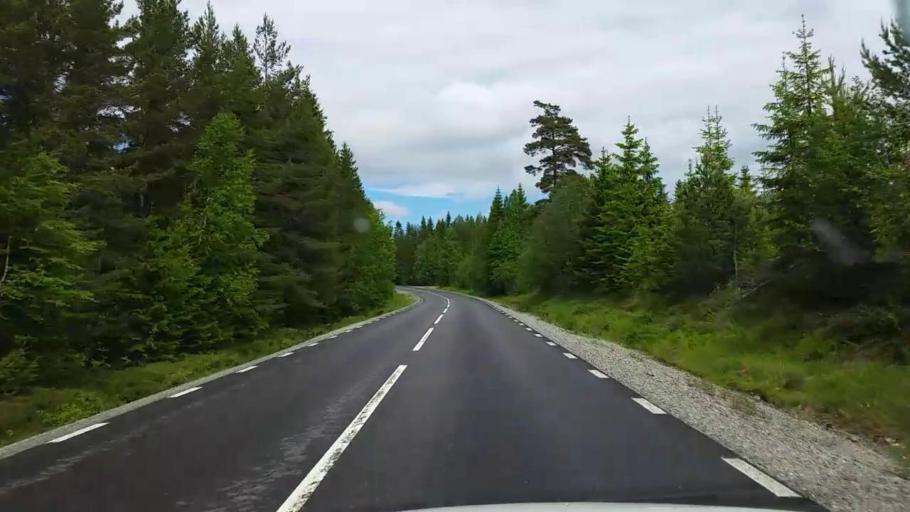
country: SE
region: Gaevleborg
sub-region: Sandvikens Kommun
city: Jarbo
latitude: 60.9000
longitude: 16.3768
